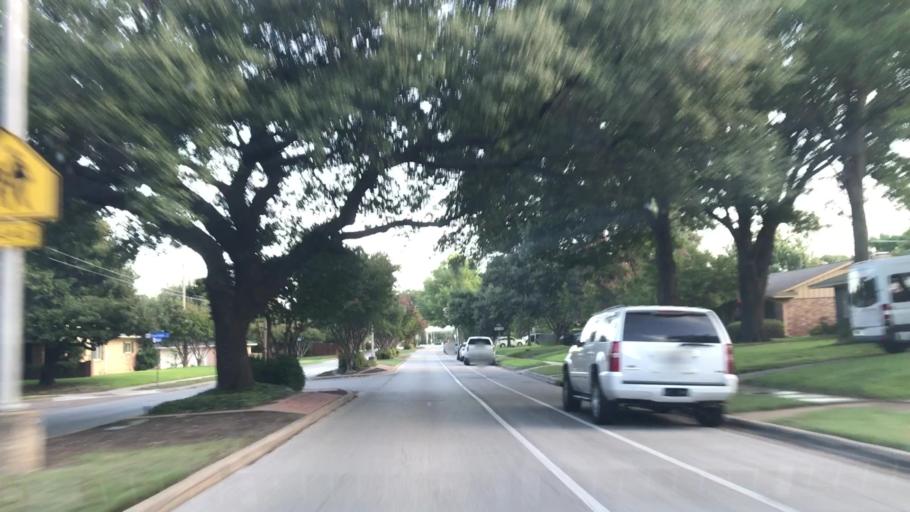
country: US
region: Texas
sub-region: Dallas County
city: Richardson
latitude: 32.9455
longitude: -96.7574
